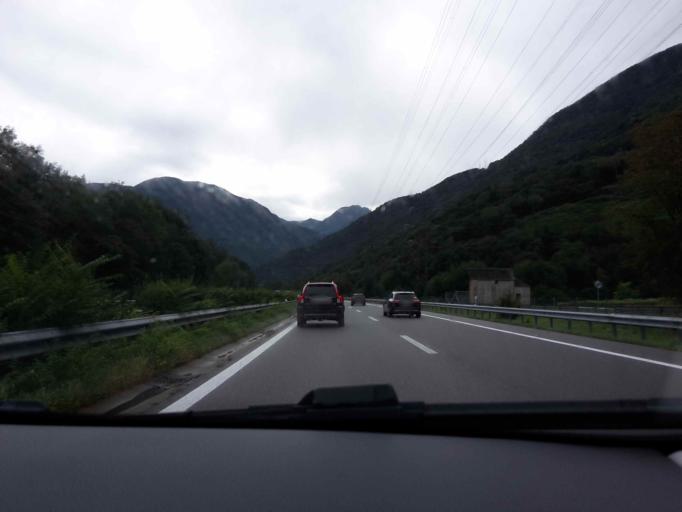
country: CH
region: Ticino
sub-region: Riviera District
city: Claro
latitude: 46.2501
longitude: 9.0108
